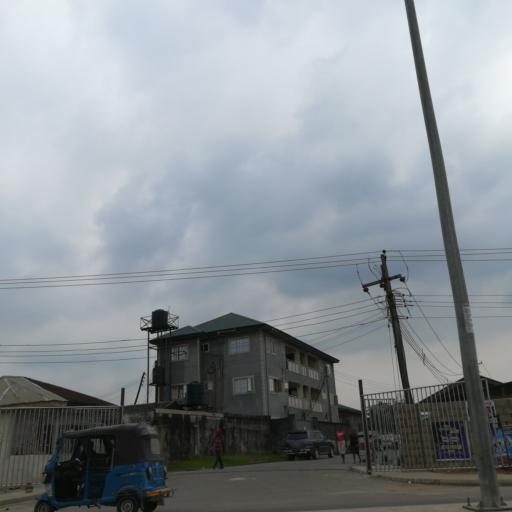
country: NG
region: Rivers
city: Port Harcourt
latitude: 4.8409
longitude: 7.0681
